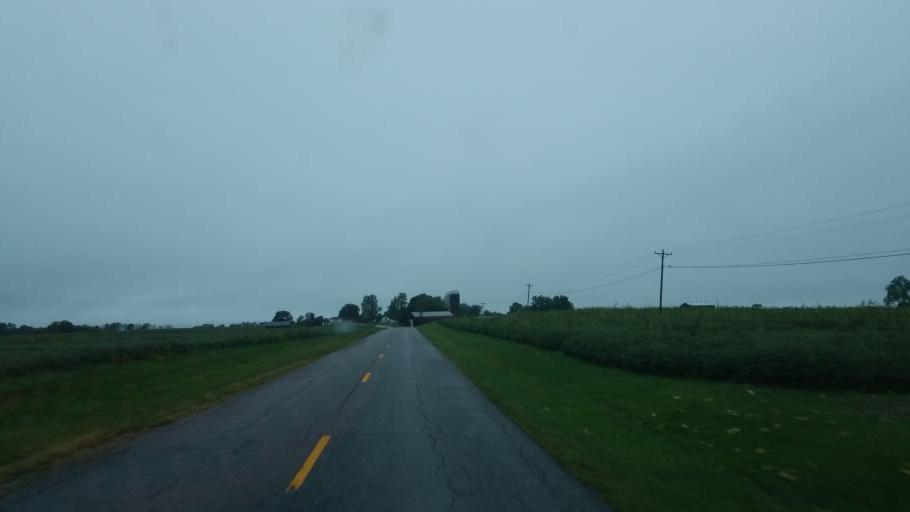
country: US
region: Kentucky
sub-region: Fleming County
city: Flemingsburg
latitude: 38.4109
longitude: -83.6555
